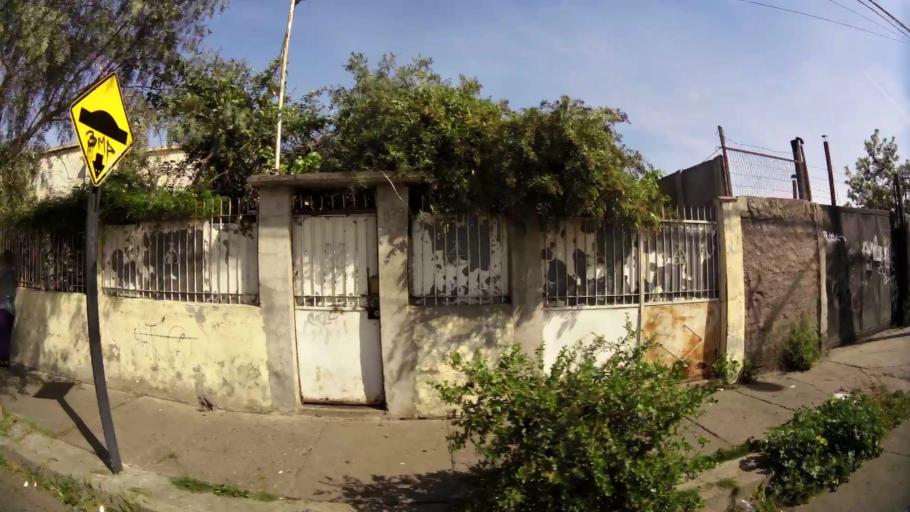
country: CL
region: Santiago Metropolitan
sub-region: Provincia de Santiago
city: La Pintana
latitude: -33.5407
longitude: -70.6334
